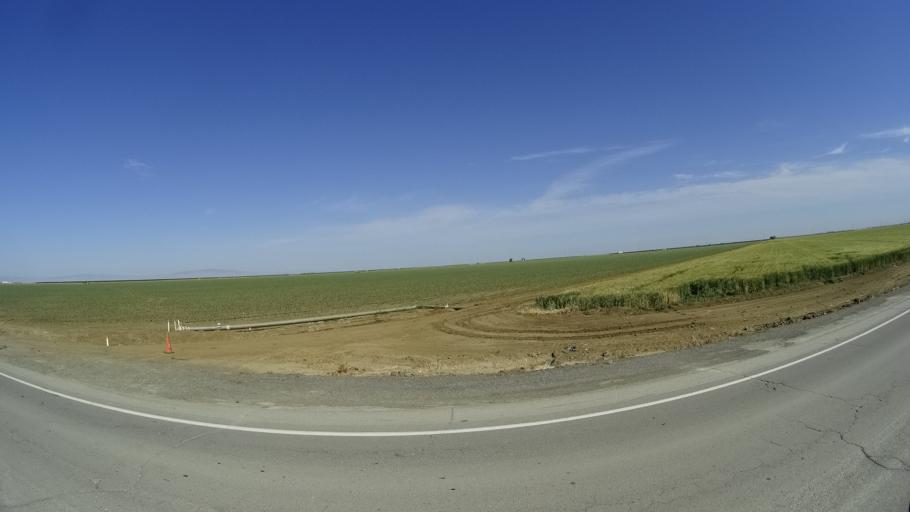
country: US
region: California
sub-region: Kings County
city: Lemoore Station
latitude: 36.1998
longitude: -119.9321
